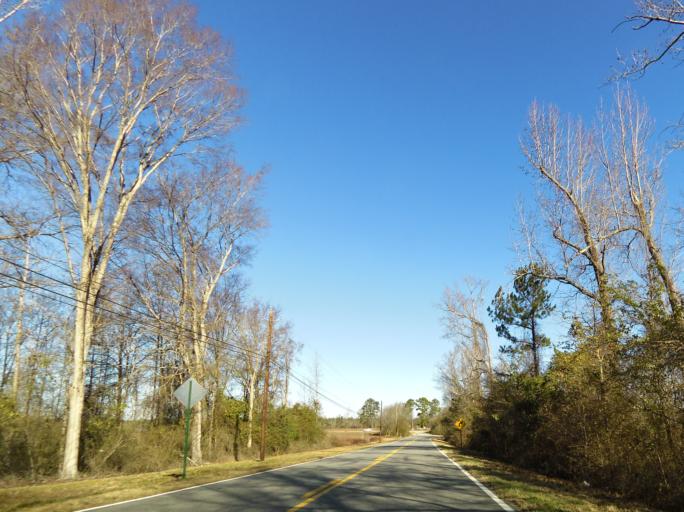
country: US
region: Georgia
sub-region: Bibb County
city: West Point
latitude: 32.7909
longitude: -83.7583
